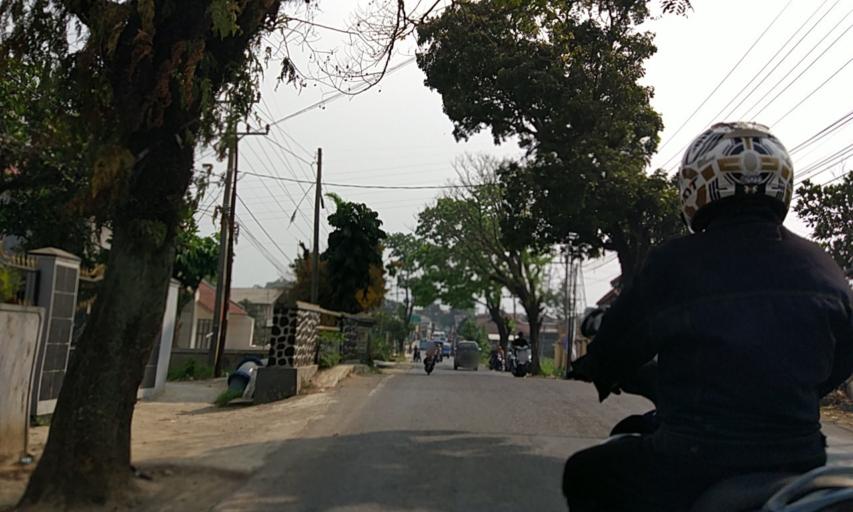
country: ID
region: West Java
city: Banjaran
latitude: -7.0439
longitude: 107.5617
